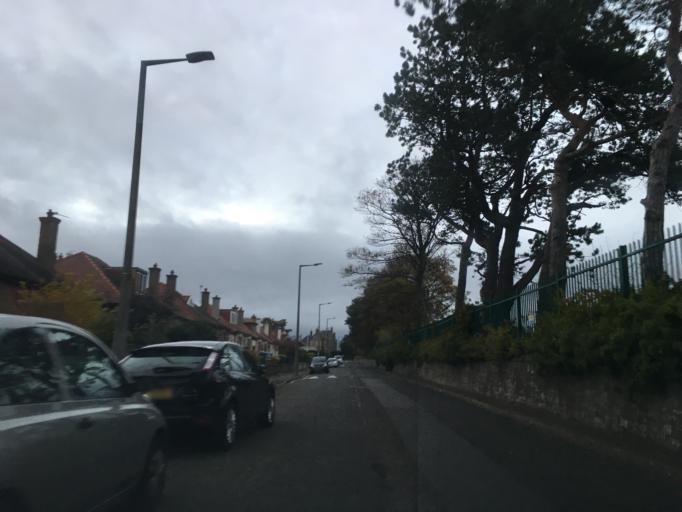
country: GB
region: Scotland
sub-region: Midlothian
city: Loanhead
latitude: 55.9069
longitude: -3.1671
